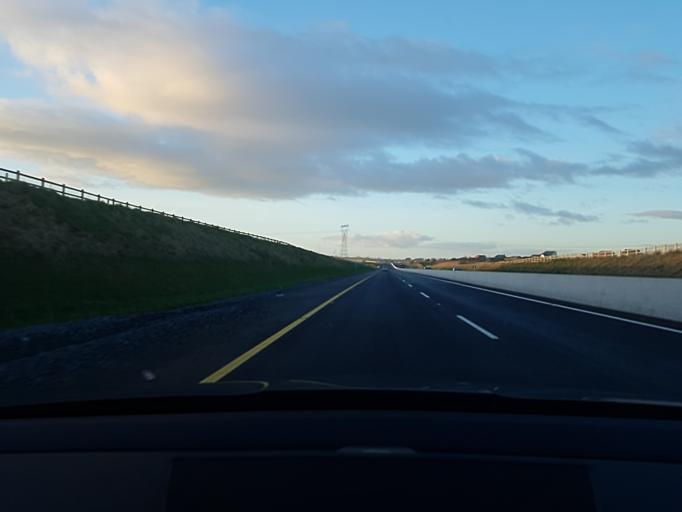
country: IE
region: Connaught
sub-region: County Galway
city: Athenry
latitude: 53.3775
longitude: -8.7960
